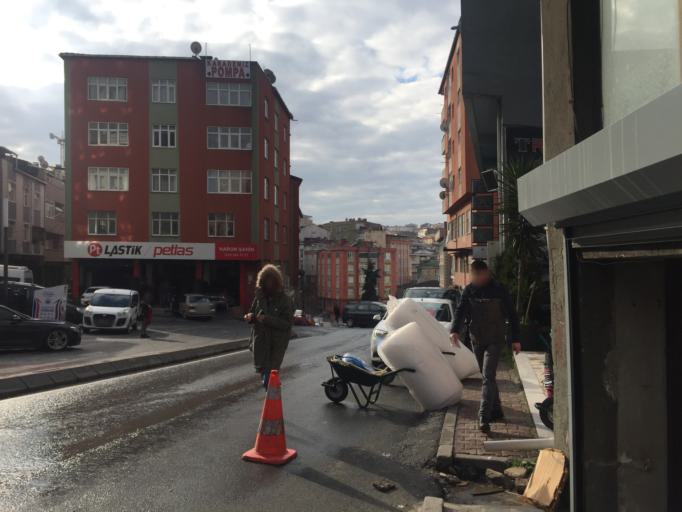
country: TR
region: Istanbul
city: Sisli
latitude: 41.0985
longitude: 28.9979
